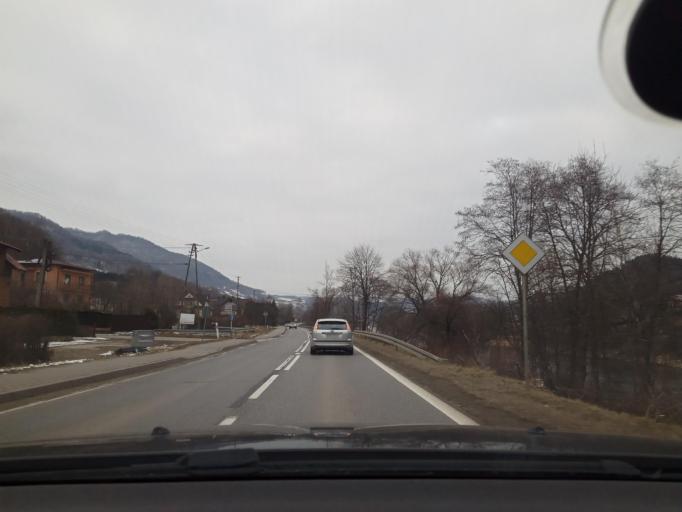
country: PL
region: Lesser Poland Voivodeship
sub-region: Powiat nowotarski
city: Kroscienko nad Dunajcem
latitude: 49.4858
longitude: 20.4104
